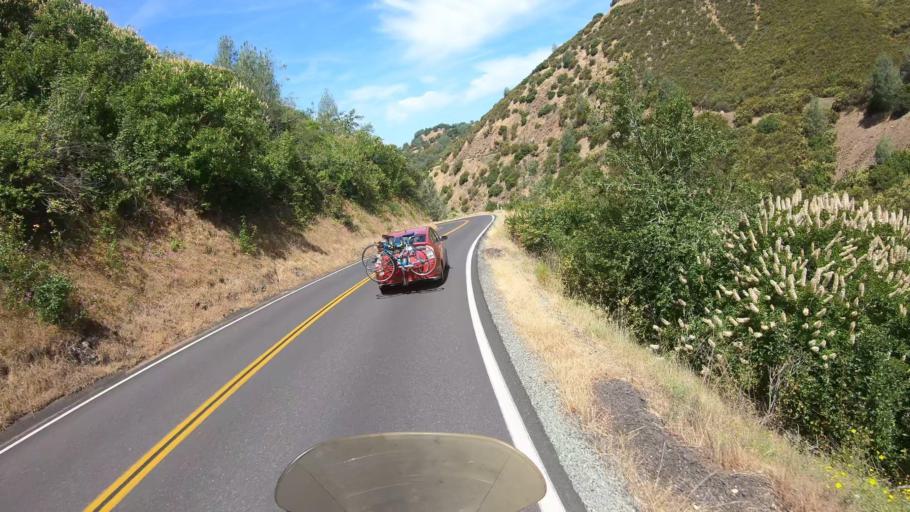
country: US
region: California
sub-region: Tuolumne County
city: Tuolumne City
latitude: 37.8162
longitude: -120.2932
